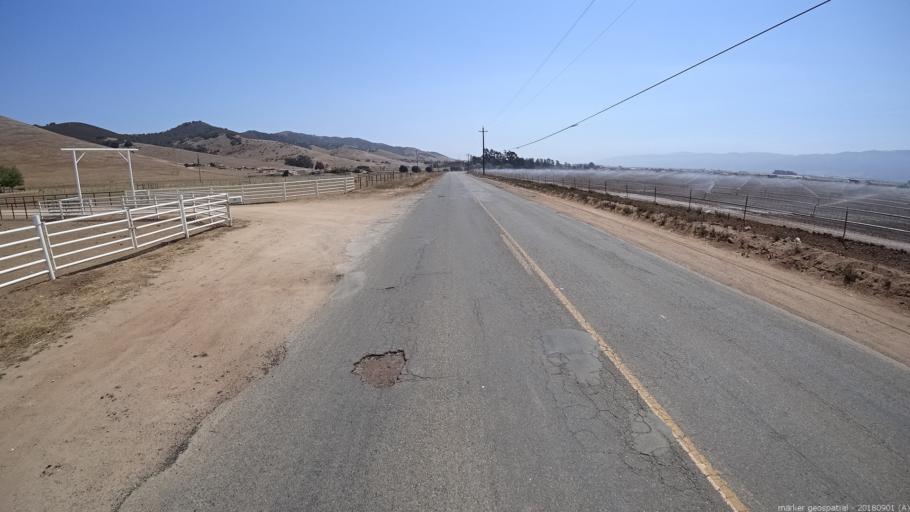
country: US
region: California
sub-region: Monterey County
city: Salinas
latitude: 36.6822
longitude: -121.5590
